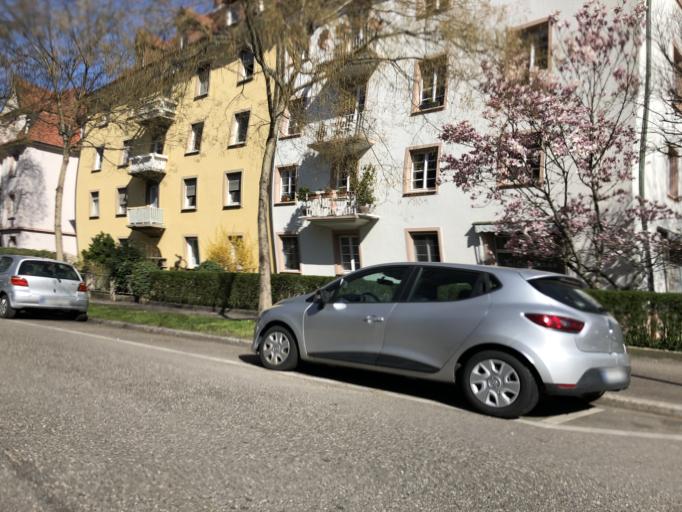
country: DE
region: Baden-Wuerttemberg
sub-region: Freiburg Region
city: Freiburg
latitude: 47.9942
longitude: 7.8281
